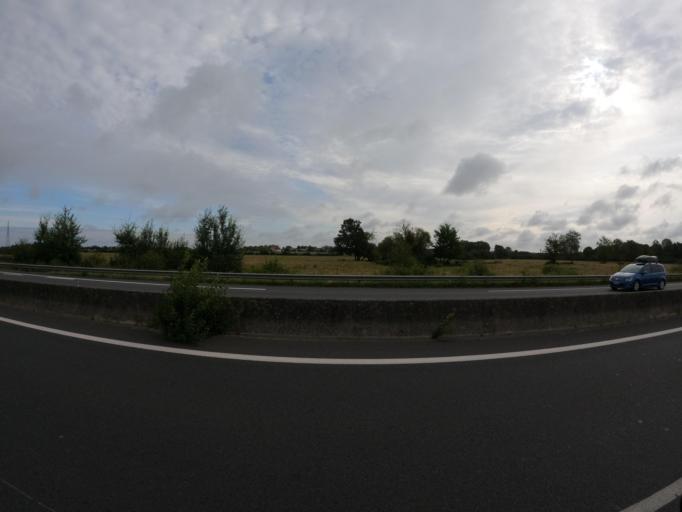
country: FR
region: Centre
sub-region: Departement d'Indre-et-Loire
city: Villandry
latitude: 47.3084
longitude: 0.5137
